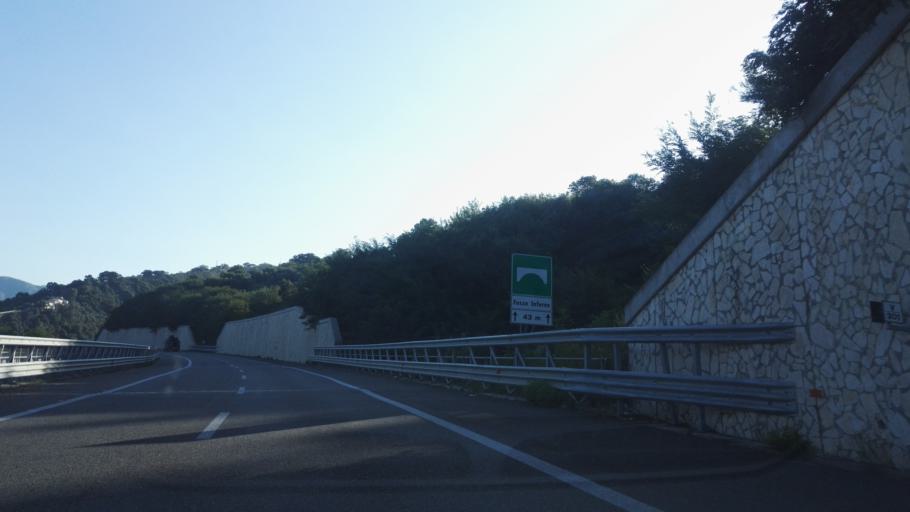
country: IT
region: Calabria
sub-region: Provincia di Catanzaro
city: Nocera Scalo
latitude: 39.0314
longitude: 16.1323
